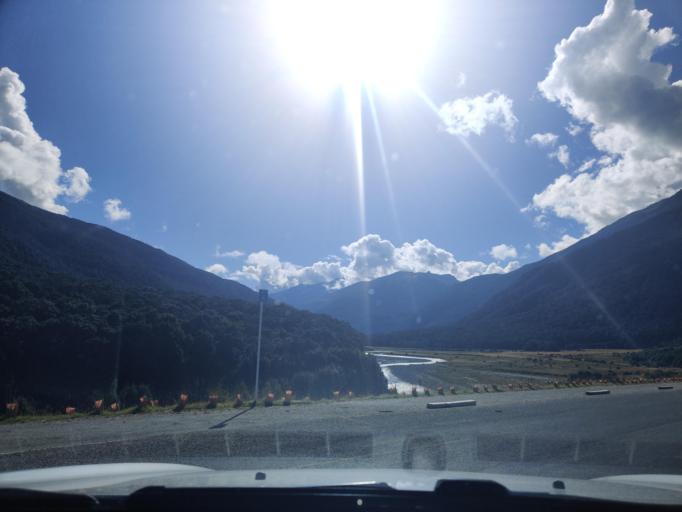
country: NZ
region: Otago
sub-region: Queenstown-Lakes District
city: Wanaka
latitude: -44.1602
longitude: 169.2862
